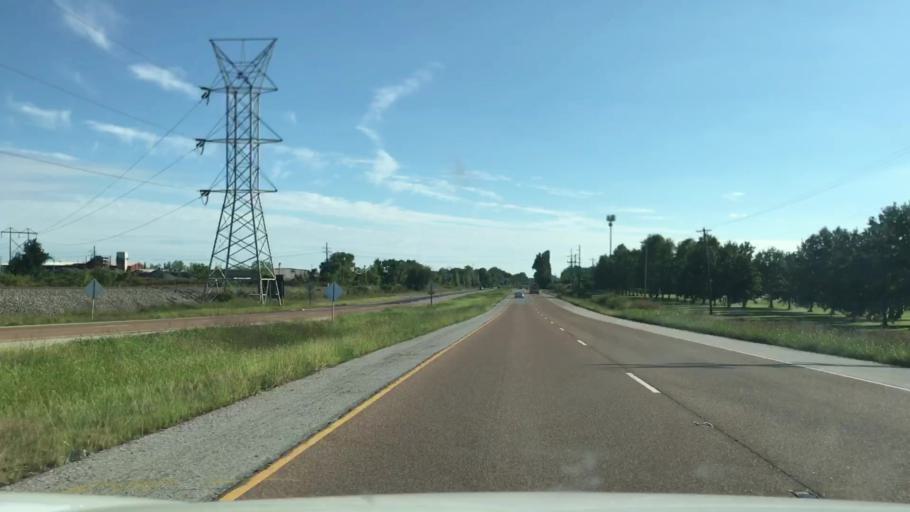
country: US
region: Illinois
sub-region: Madison County
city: Hartford
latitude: 38.8025
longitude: -90.1003
